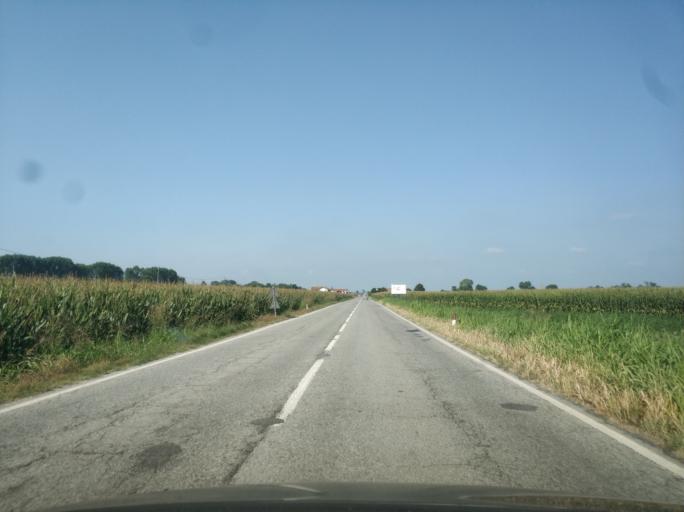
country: IT
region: Piedmont
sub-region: Provincia di Cuneo
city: Centallo
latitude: 44.5288
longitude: 7.6058
